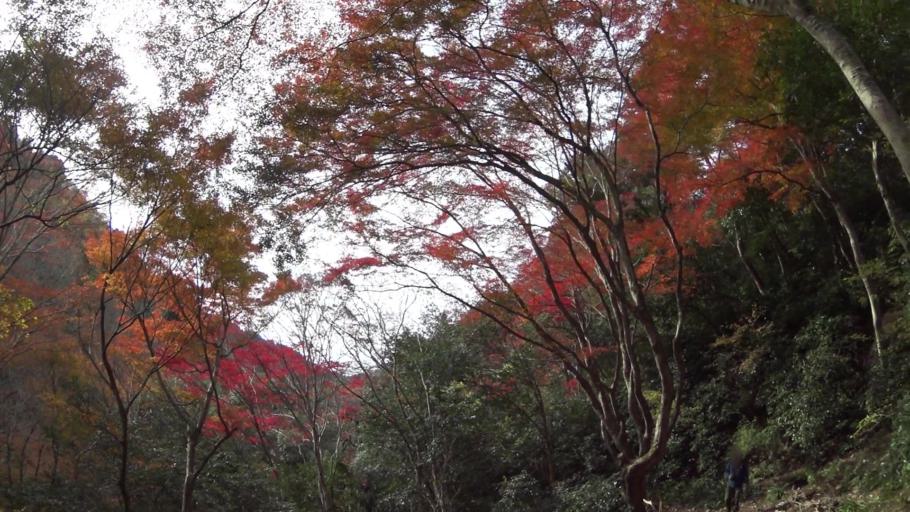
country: JP
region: Hyogo
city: Takarazuka
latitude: 34.8534
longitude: 135.3205
